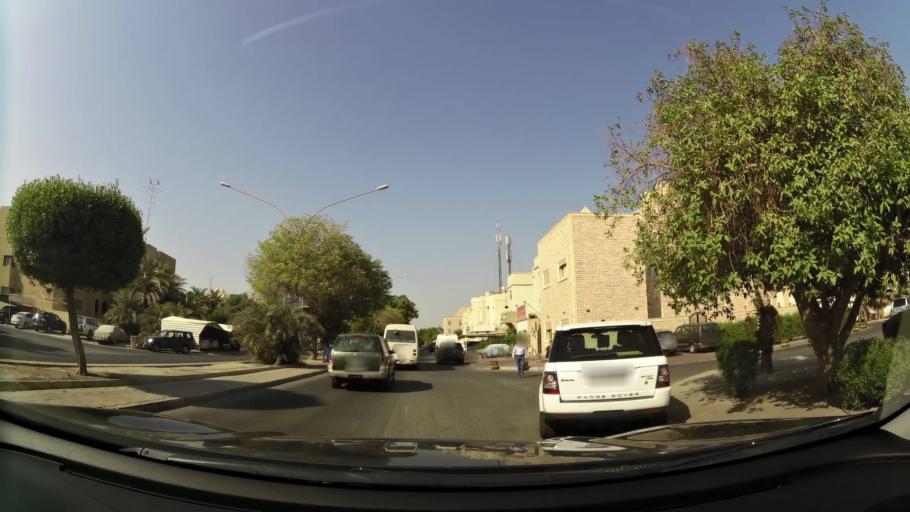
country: KW
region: Muhafazat Hawalli
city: Salwa
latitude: 29.2941
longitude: 48.0832
